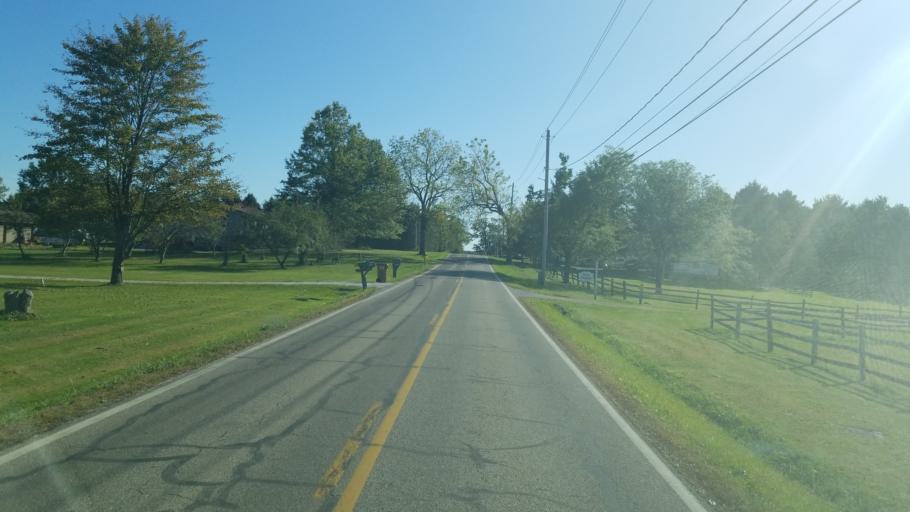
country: US
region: Ohio
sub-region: Medina County
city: Westfield Center
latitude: 41.0138
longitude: -81.9109
